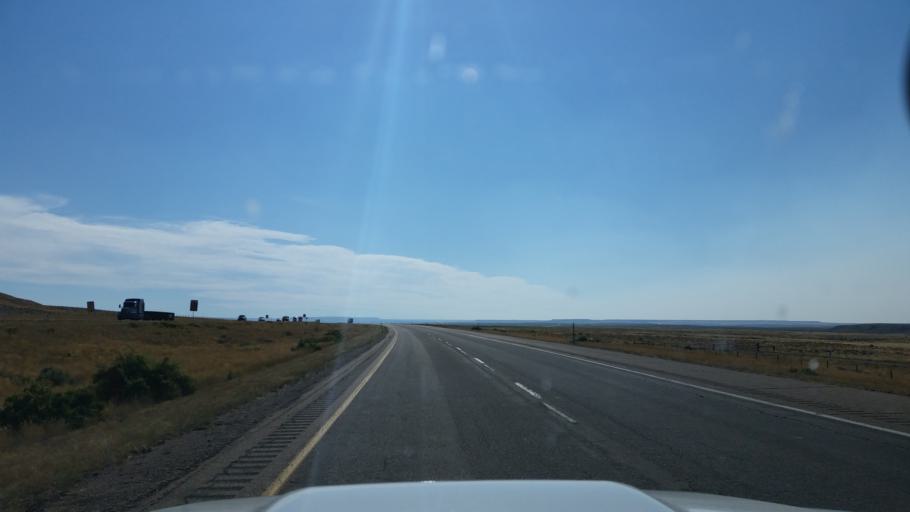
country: US
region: Wyoming
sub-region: Uinta County
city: Lyman
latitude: 41.3856
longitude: -110.2185
